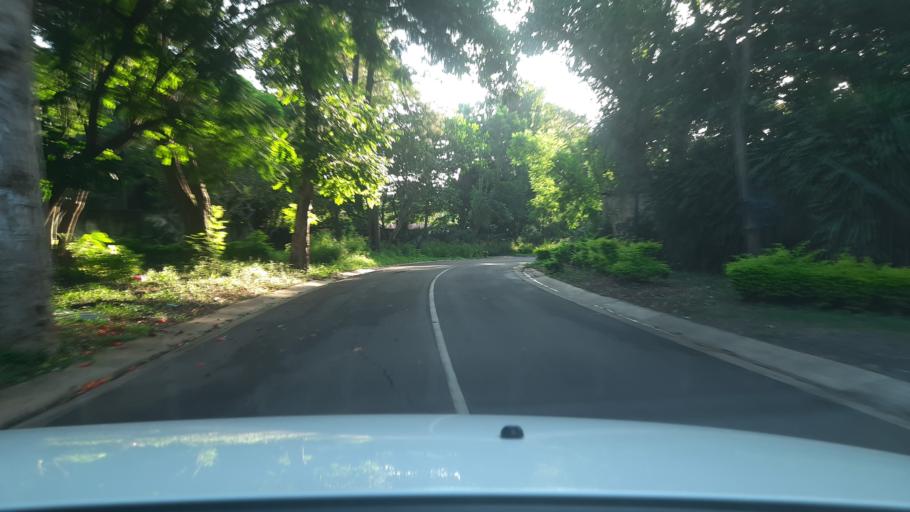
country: TZ
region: Arusha
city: Arusha
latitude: -3.3803
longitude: 36.6981
